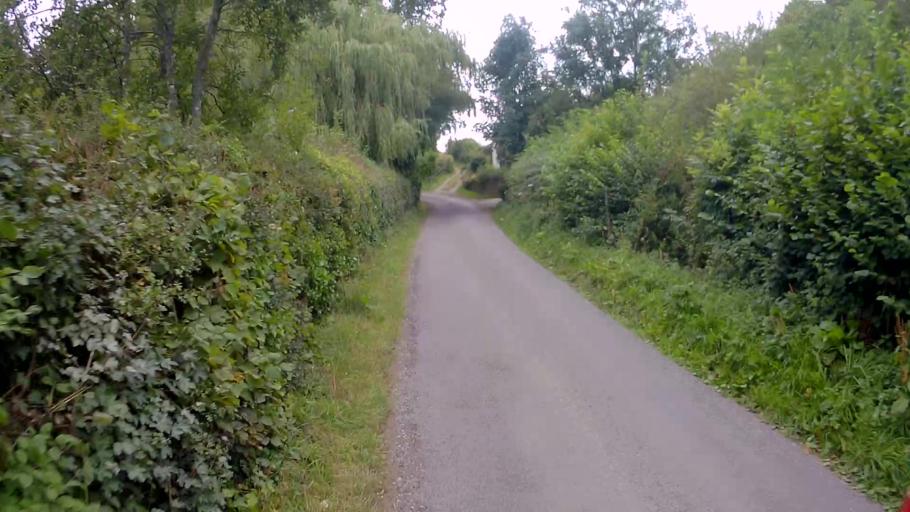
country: GB
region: England
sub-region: Hampshire
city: Kings Worthy
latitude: 51.1649
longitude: -1.3309
